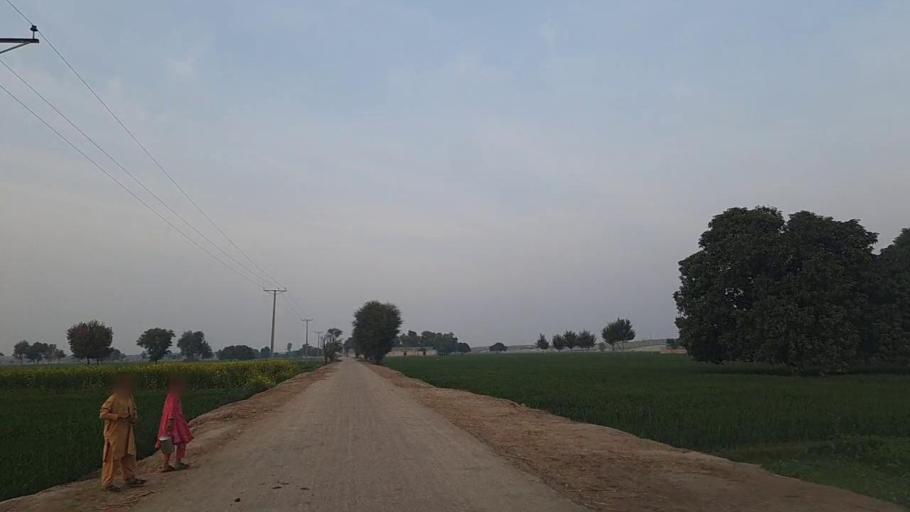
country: PK
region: Sindh
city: Jam Sahib
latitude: 26.4689
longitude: 68.5481
